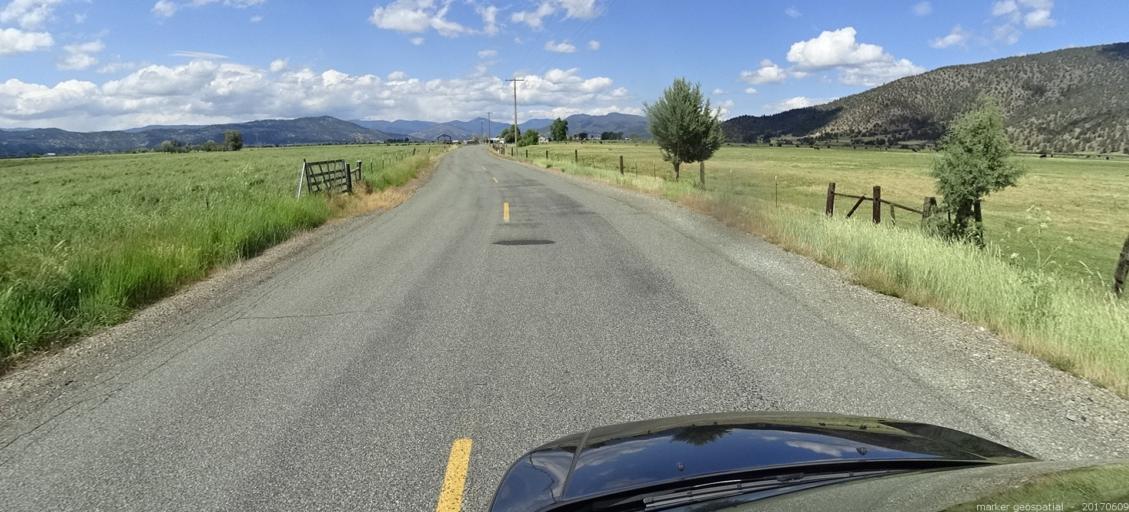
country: US
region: California
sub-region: Siskiyou County
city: Yreka
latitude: 41.5063
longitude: -122.8568
